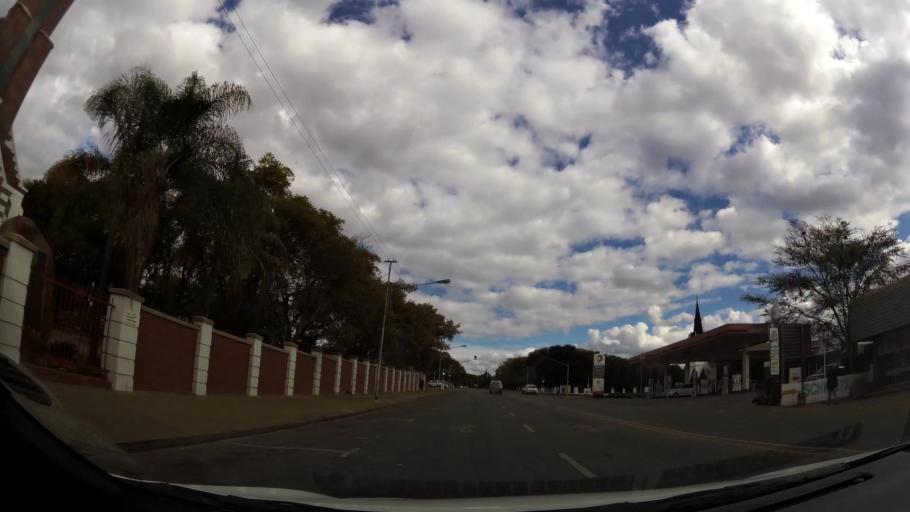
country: ZA
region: Limpopo
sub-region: Waterberg District Municipality
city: Modimolle
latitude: -24.7009
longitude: 28.4048
